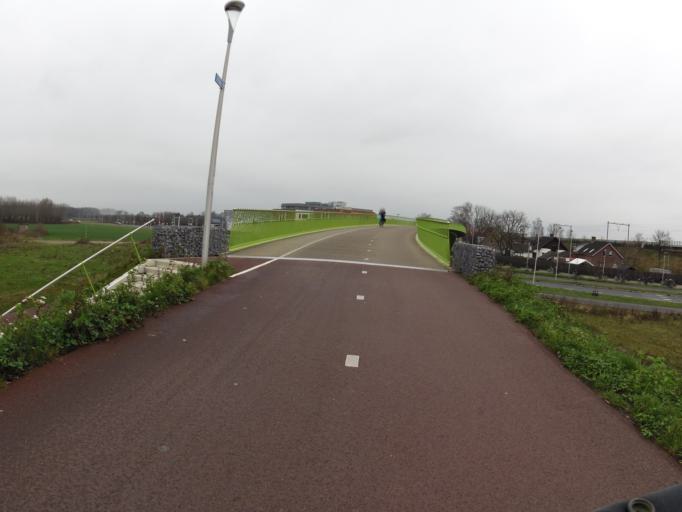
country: NL
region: Gelderland
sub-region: Gemeente Nijmegen
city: Nijmegen
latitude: 51.8632
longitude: 5.8584
